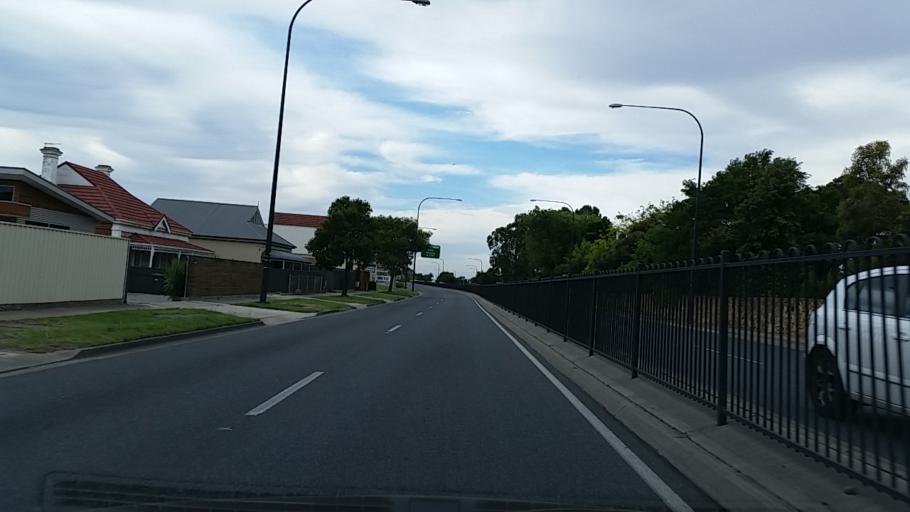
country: AU
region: South Australia
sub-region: Unley
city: Forestville
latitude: -34.9581
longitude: 138.5723
